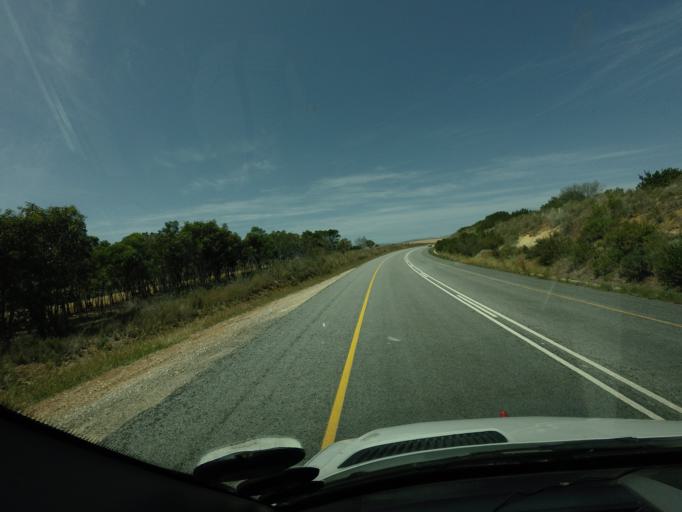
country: ZA
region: Western Cape
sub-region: Overberg District Municipality
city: Hermanus
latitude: -34.3143
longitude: 19.1488
